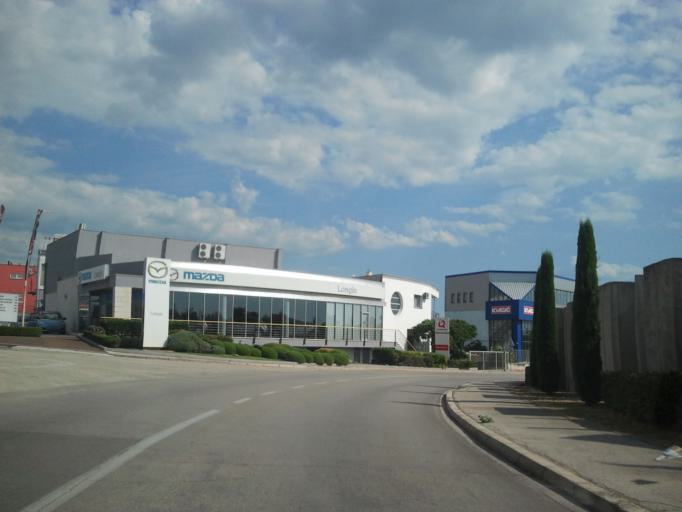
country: HR
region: Zadarska
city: Zadar
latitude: 44.1049
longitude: 15.2610
